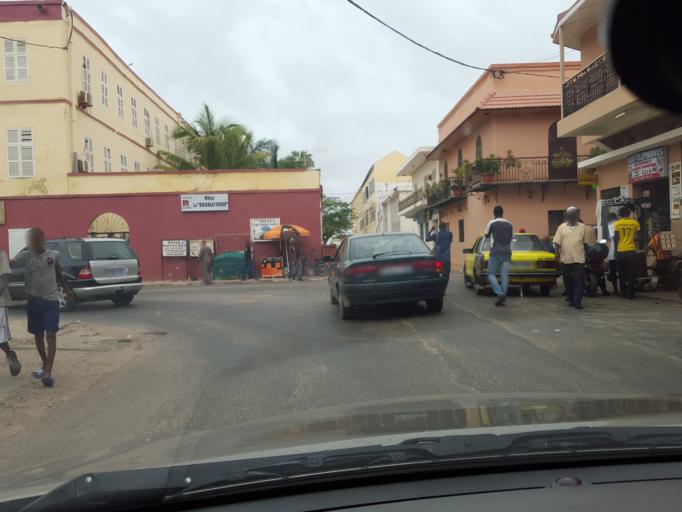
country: SN
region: Saint-Louis
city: Saint-Louis
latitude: 16.0263
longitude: -16.5047
